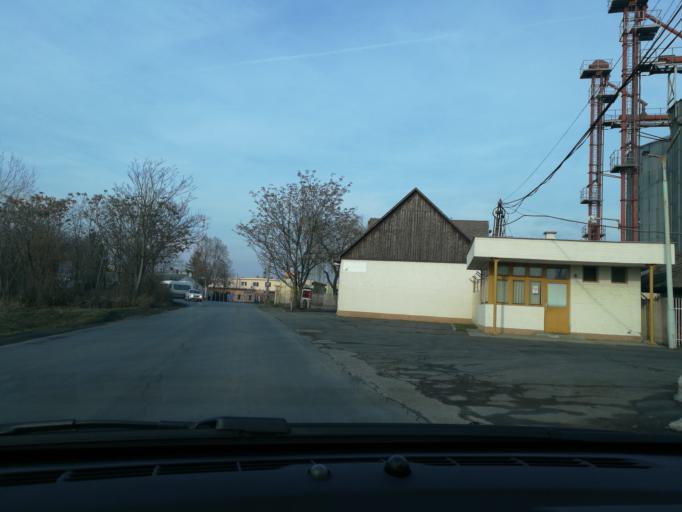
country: HU
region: Szabolcs-Szatmar-Bereg
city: Nyiregyhaza
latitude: 47.9366
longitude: 21.7125
